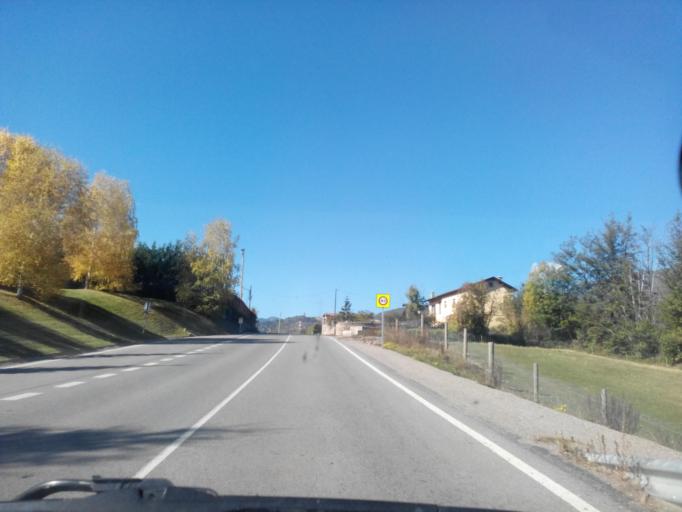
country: ES
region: Catalonia
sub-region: Provincia de Lleida
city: Bellver de Cerdanya
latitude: 42.3691
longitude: 1.7861
